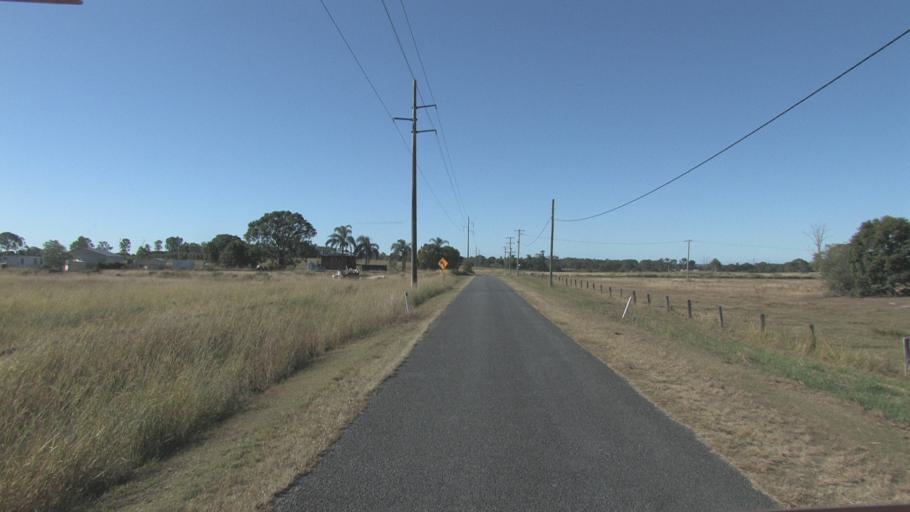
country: AU
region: Queensland
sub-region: Logan
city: Chambers Flat
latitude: -27.7675
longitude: 153.0616
